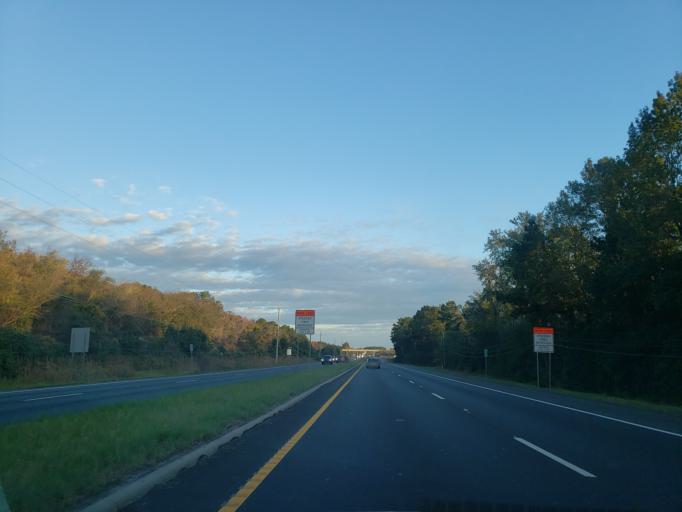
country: US
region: Georgia
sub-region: Chatham County
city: Port Wentworth
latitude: 32.1566
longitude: -81.1817
